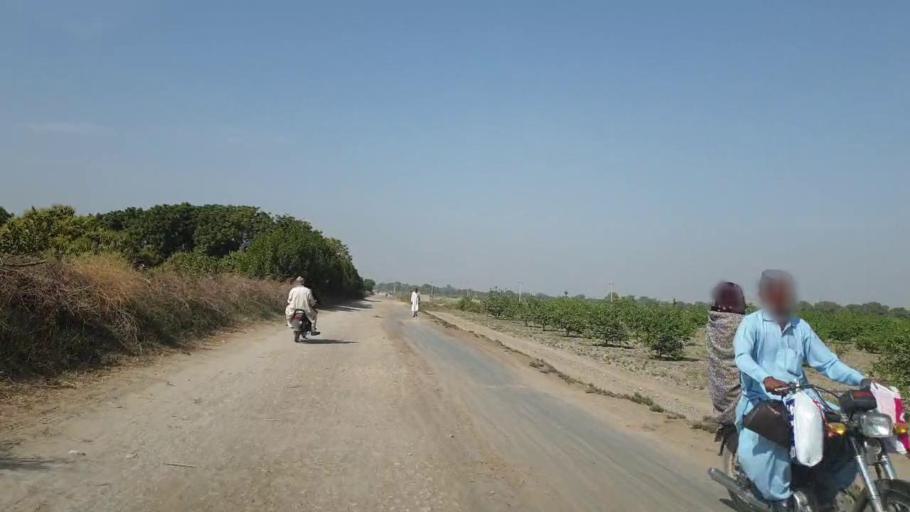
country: PK
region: Sindh
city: Nabisar
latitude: 25.0285
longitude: 69.5244
